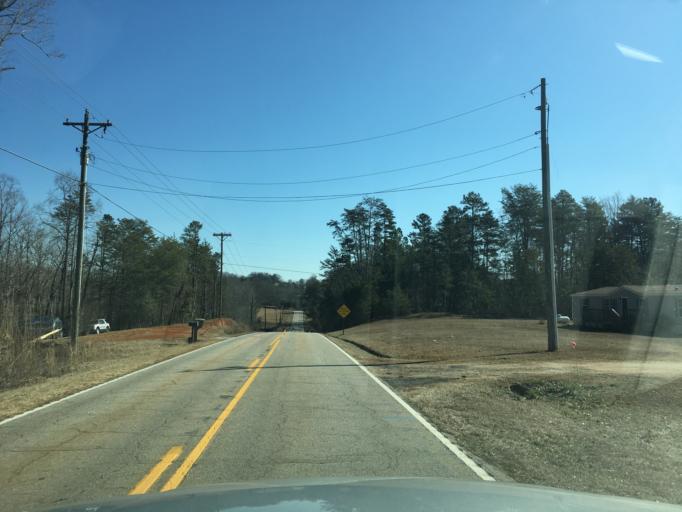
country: US
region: South Carolina
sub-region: Pickens County
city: Liberty
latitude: 34.8033
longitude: -82.7522
